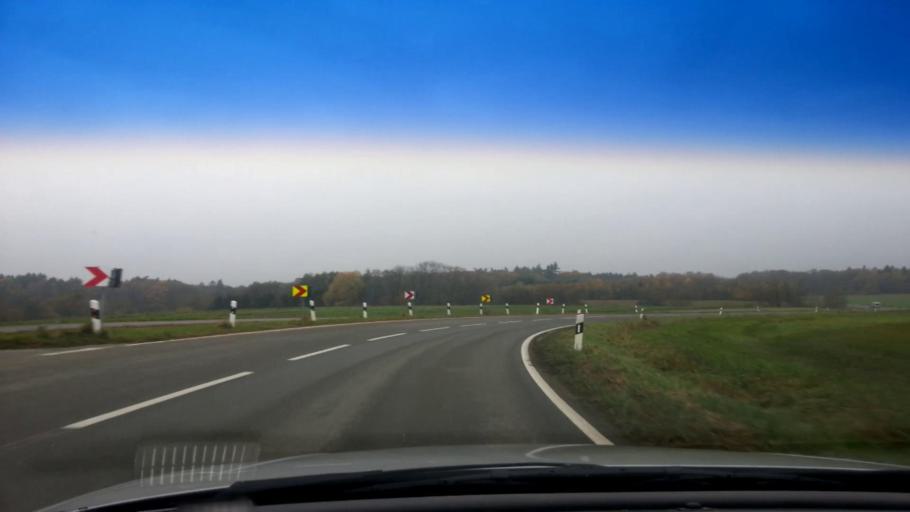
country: DE
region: Bavaria
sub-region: Upper Franconia
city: Litzendorf
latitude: 49.8861
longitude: 11.0107
